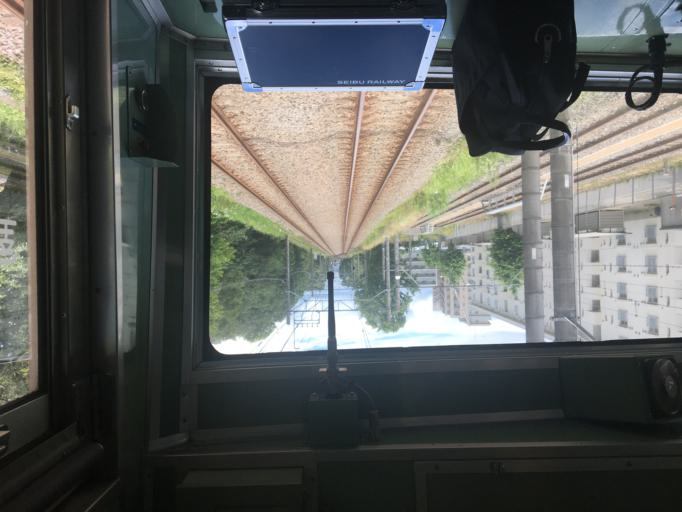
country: JP
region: Tokyo
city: Higashimurayama-shi
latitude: 35.7428
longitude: 139.4726
